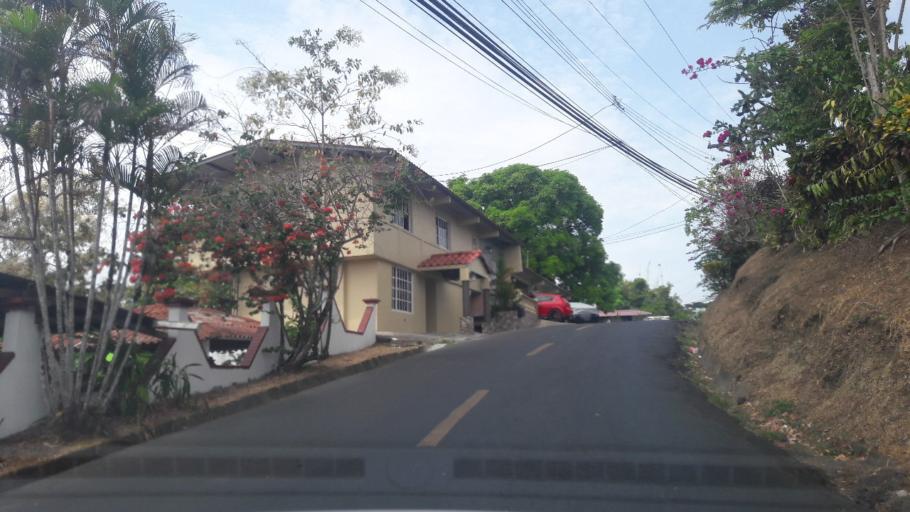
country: PA
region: Panama
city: Alcalde Diaz
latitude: 9.1197
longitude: -79.5561
